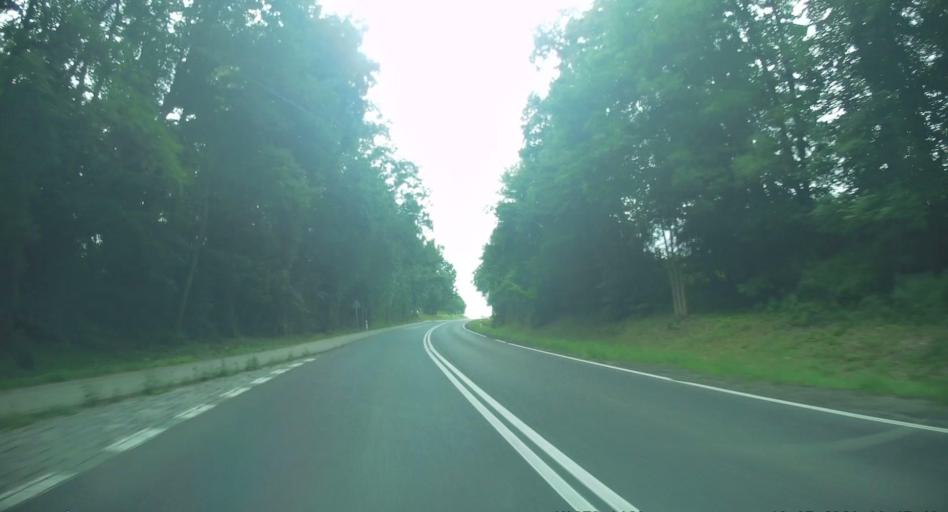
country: PL
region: Opole Voivodeship
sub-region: Powiat prudnicki
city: Laka Prudnicka
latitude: 50.4030
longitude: 17.5099
